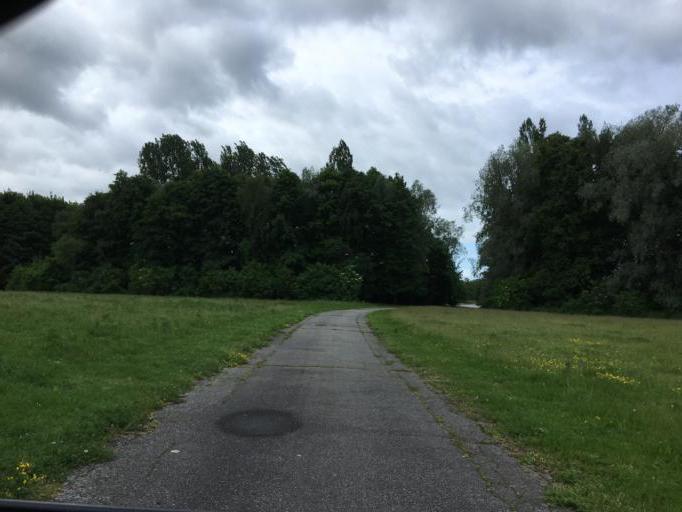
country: SE
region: Skane
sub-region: Burlovs Kommun
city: Arloev
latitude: 55.5742
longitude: 13.0530
